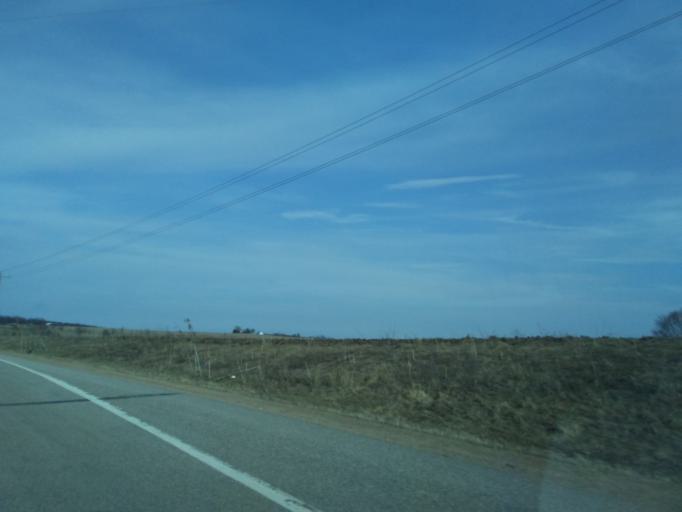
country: US
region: Wisconsin
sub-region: Grant County
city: Fennimore
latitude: 42.9819
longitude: -90.7246
